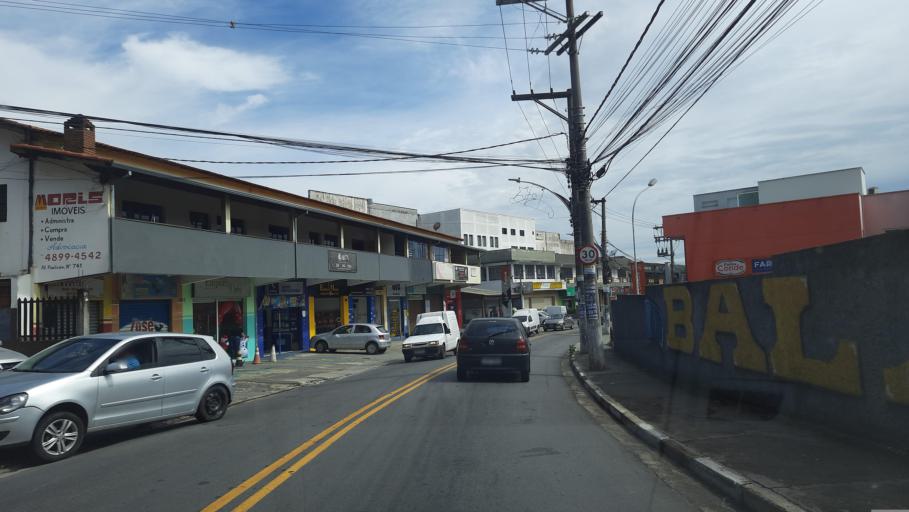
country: BR
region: Sao Paulo
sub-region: Caieiras
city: Caieiras
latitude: -23.3927
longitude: -46.7159
